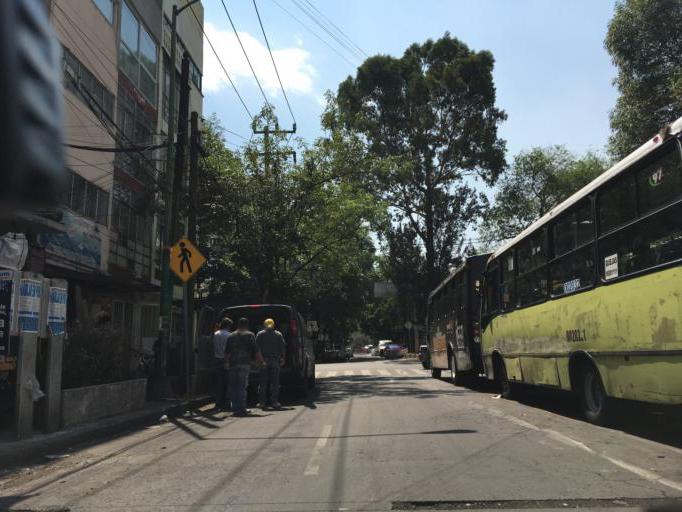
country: MX
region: Mexico City
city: Polanco
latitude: 19.4200
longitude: -99.1764
